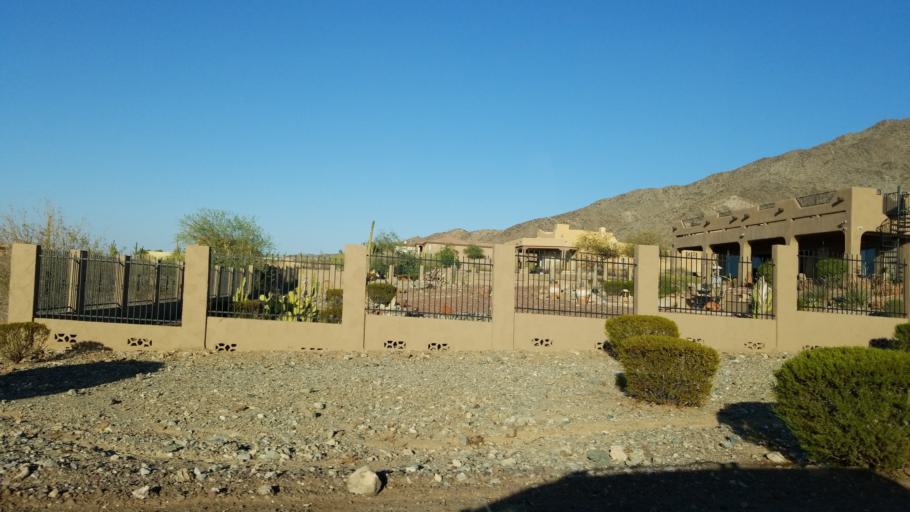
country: US
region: Arizona
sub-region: Maricopa County
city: Laveen
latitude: 33.3491
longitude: -112.1176
